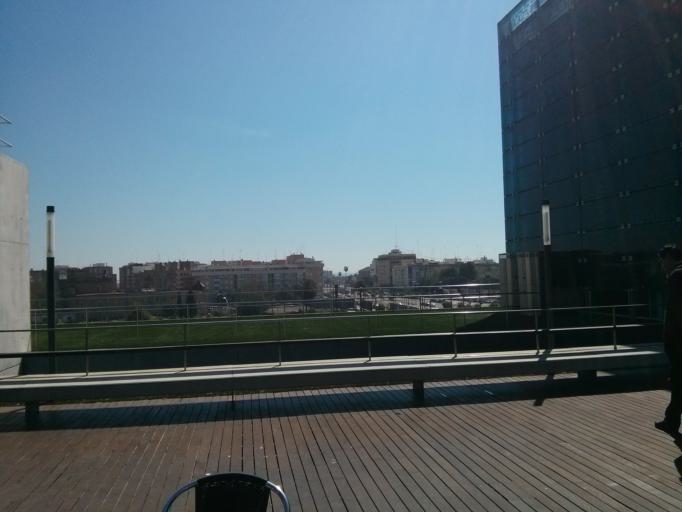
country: ES
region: Valencia
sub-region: Provincia de Valencia
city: Alboraya
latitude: 39.4772
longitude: -0.3342
